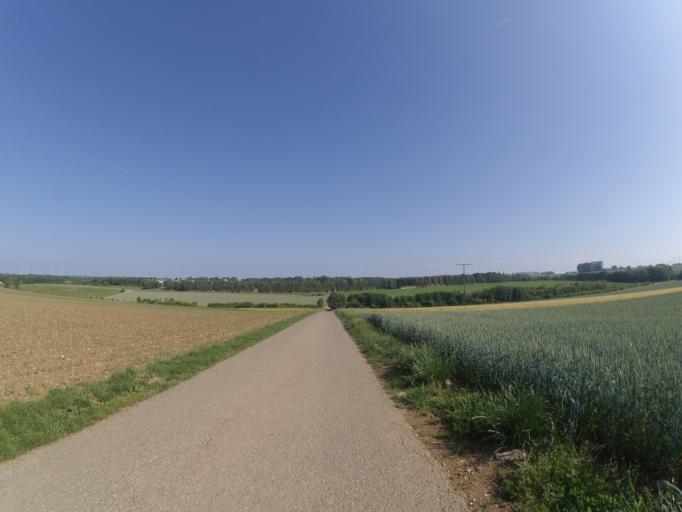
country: DE
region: Baden-Wuerttemberg
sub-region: Tuebingen Region
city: Dornstadt
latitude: 48.4426
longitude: 9.9666
